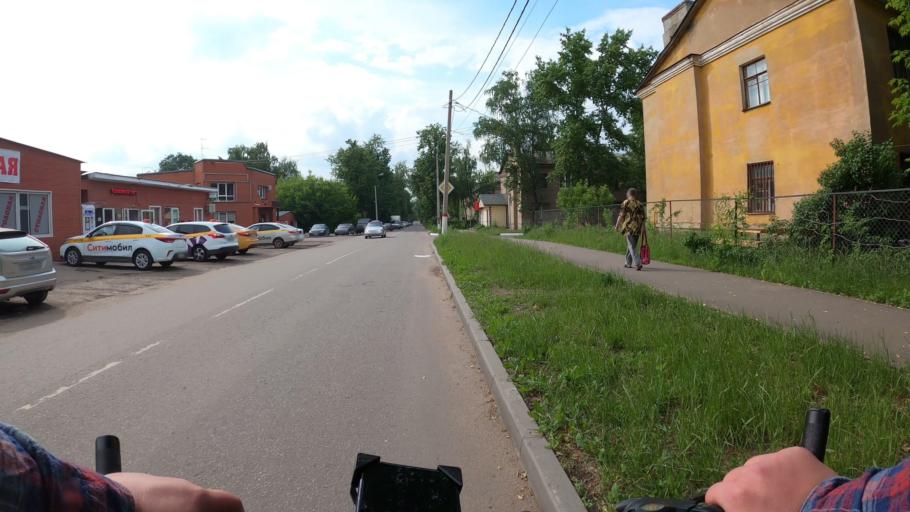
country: RU
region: Moskovskaya
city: Zhukovskiy
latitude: 55.6059
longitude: 38.1098
